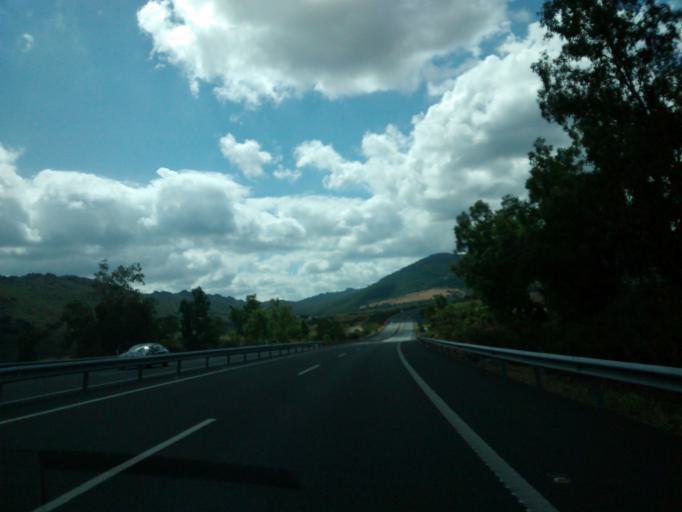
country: ES
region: Extremadura
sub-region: Provincia de Caceres
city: Romangordo
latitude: 39.7133
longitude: -5.6985
